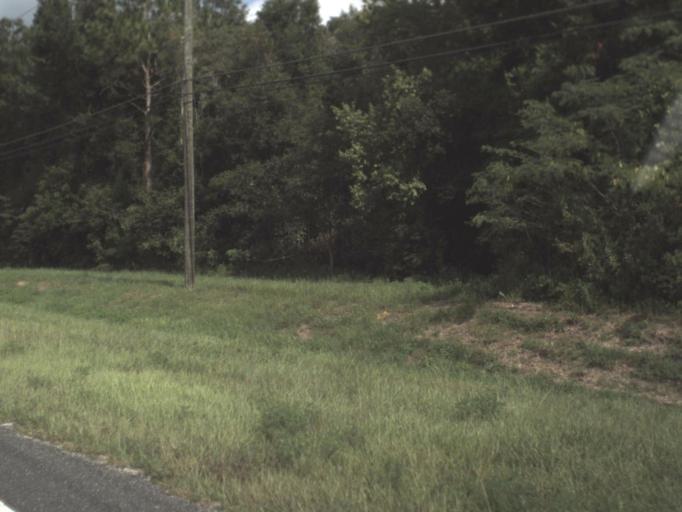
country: US
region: Florida
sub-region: Hernando County
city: Hill 'n Dale
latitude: 28.5233
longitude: -82.2515
